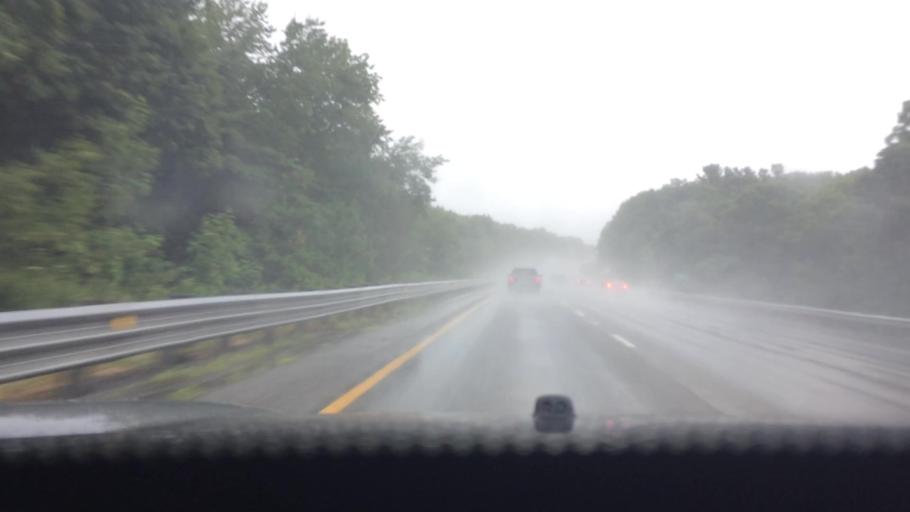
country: US
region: Massachusetts
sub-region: Worcester County
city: Harvard
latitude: 42.4928
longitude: -71.5401
